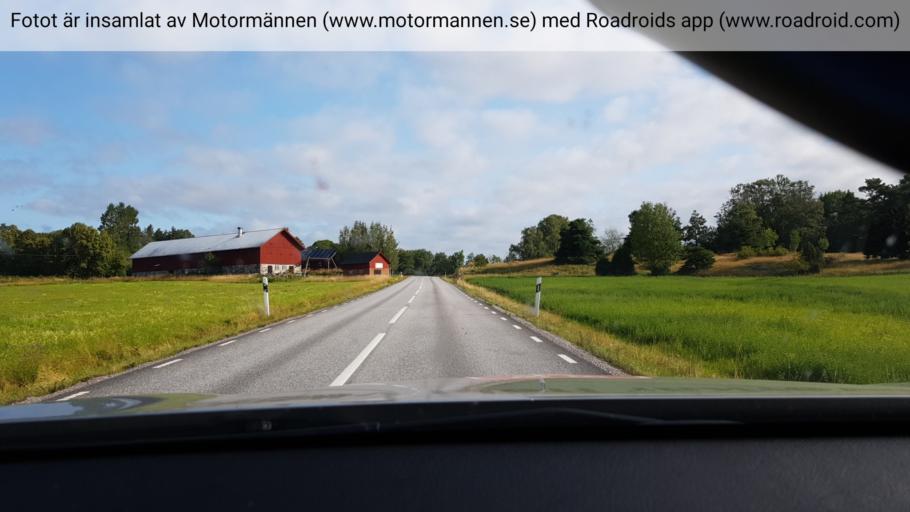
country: SE
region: Stockholm
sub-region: Norrtalje Kommun
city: Rimbo
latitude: 59.7019
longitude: 18.3731
